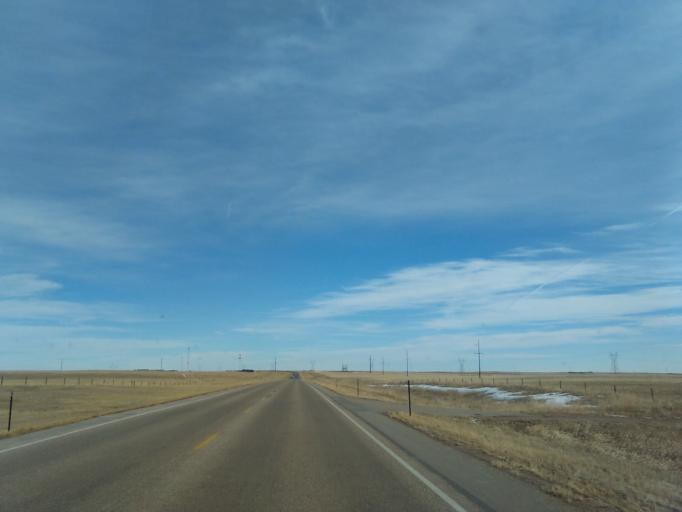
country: US
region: Wyoming
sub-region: Laramie County
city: Pine Bluffs
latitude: 41.4342
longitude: -104.3638
